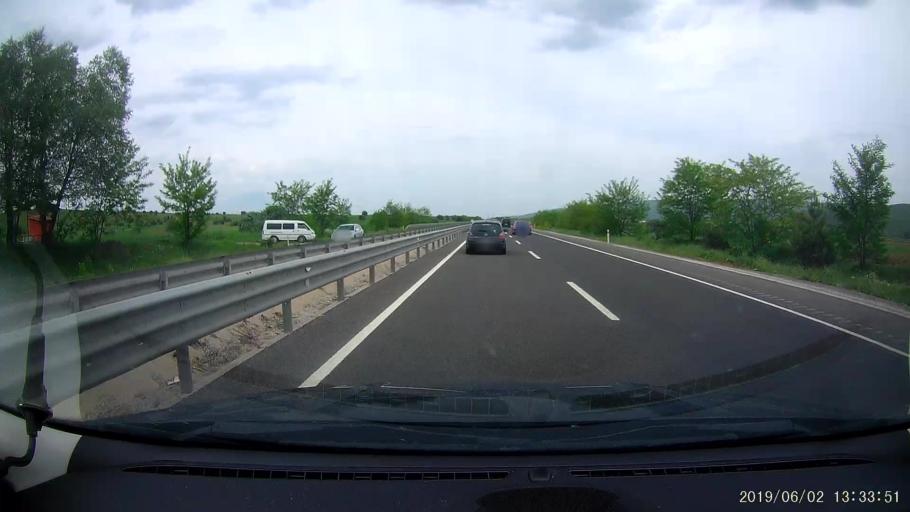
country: TR
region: Cankiri
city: Atkaracalar
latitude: 40.8014
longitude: 33.0187
